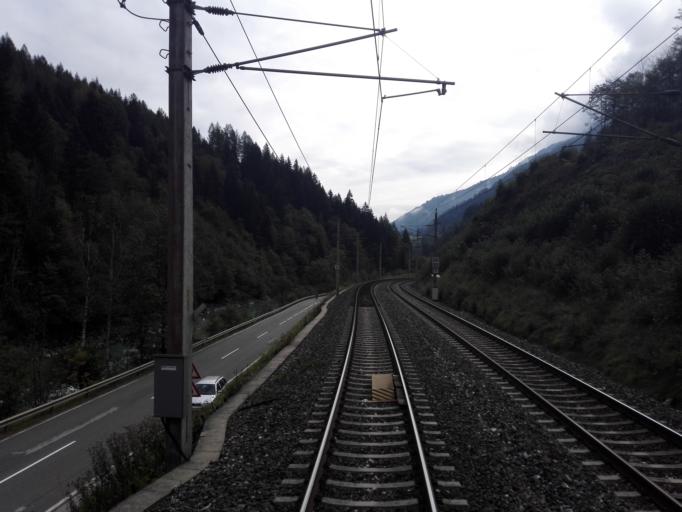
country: AT
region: Salzburg
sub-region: Politischer Bezirk Sankt Johann im Pongau
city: Goldegg
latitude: 47.3016
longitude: 13.0982
